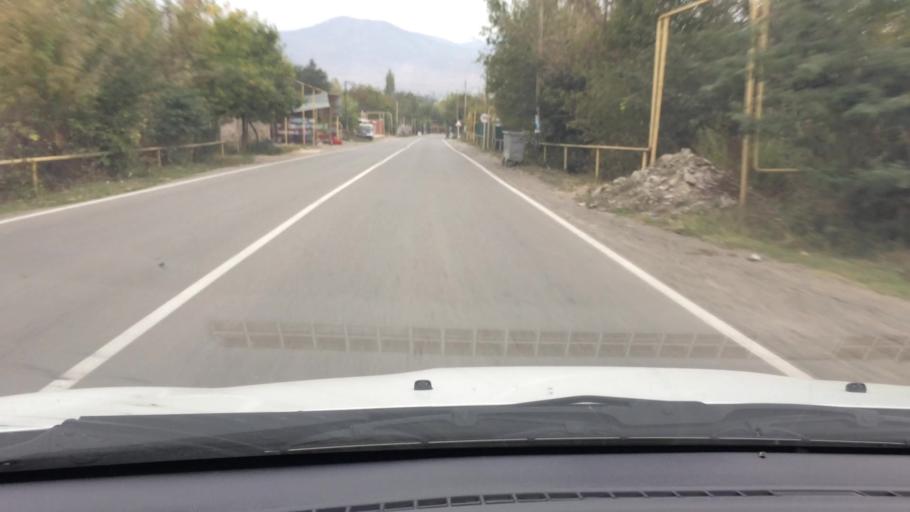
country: AM
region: Tavush
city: Bagratashen
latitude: 41.2367
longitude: 44.8057
